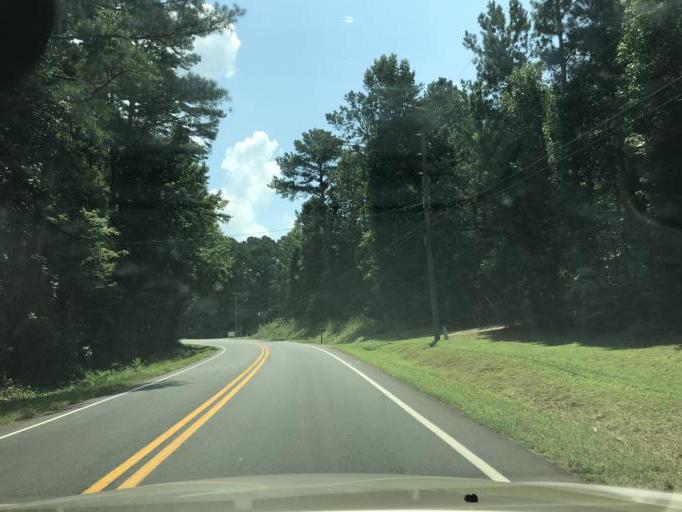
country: US
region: Georgia
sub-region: Dawson County
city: Dawsonville
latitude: 34.3359
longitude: -84.1492
